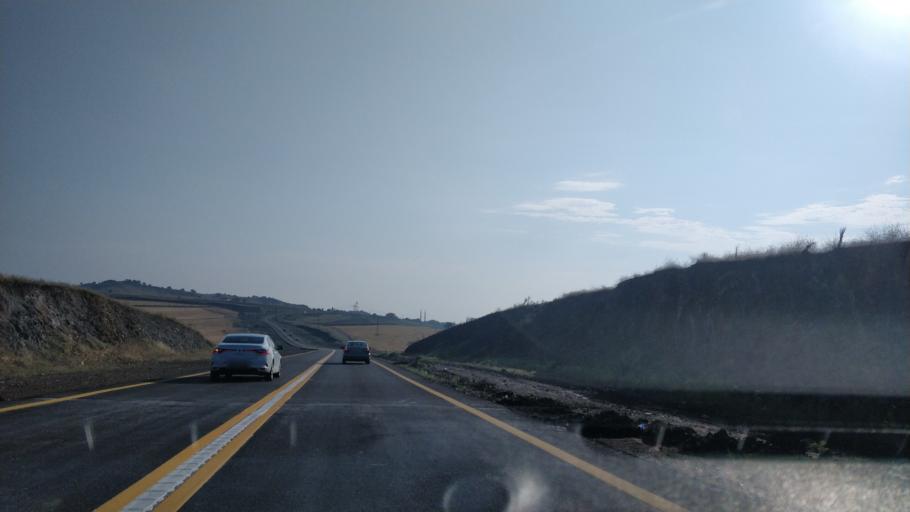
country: TR
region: Ankara
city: Etimesgut
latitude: 39.8567
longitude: 32.5683
